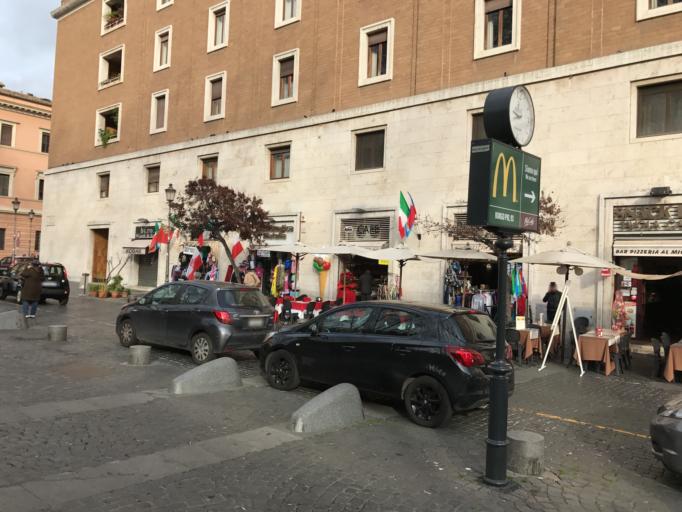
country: VA
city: Vatican City
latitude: 41.9035
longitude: 12.4584
